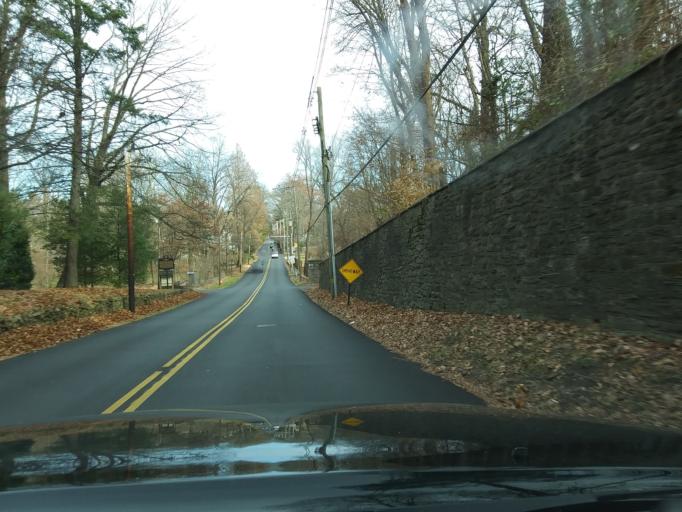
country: US
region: Pennsylvania
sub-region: Montgomery County
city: Jenkintown
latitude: 40.0931
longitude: -75.1173
